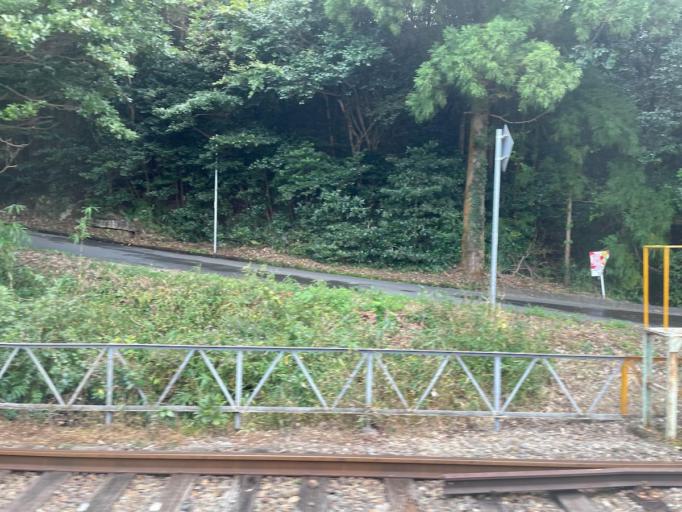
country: JP
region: Mie
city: Komono
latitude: 35.0119
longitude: 136.4755
